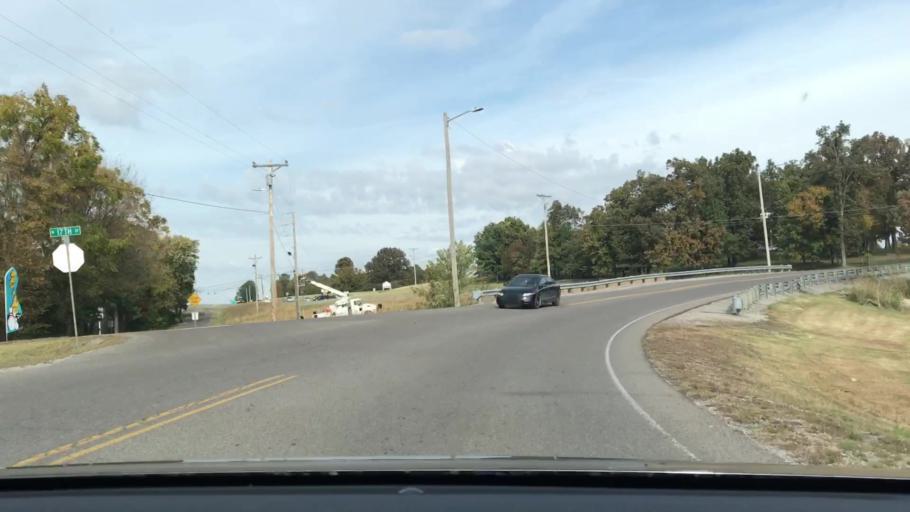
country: US
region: Kentucky
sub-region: Graves County
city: Mayfield
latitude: 36.7517
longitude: -88.6515
